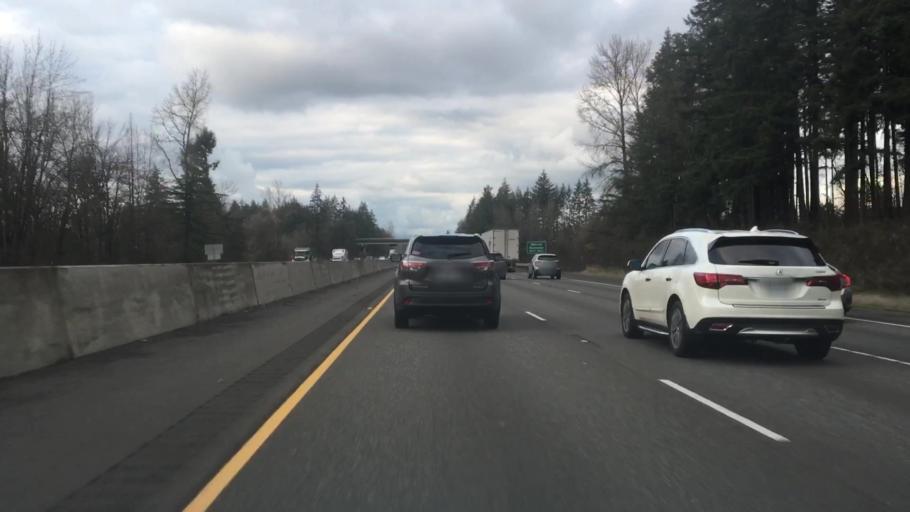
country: US
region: Washington
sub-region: Thurston County
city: Grand Mound
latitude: 46.7722
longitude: -122.9970
